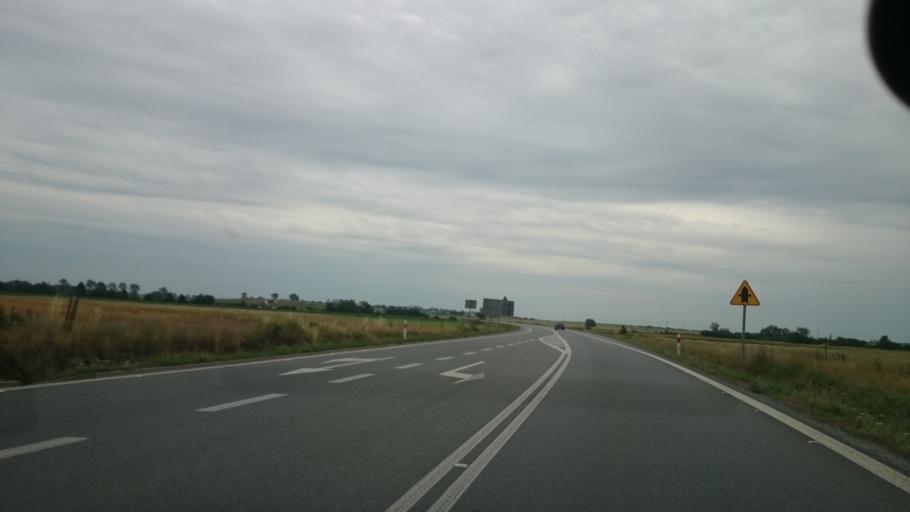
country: PL
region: Opole Voivodeship
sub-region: Powiat brzeski
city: Grodkow
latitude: 50.6891
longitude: 17.3650
